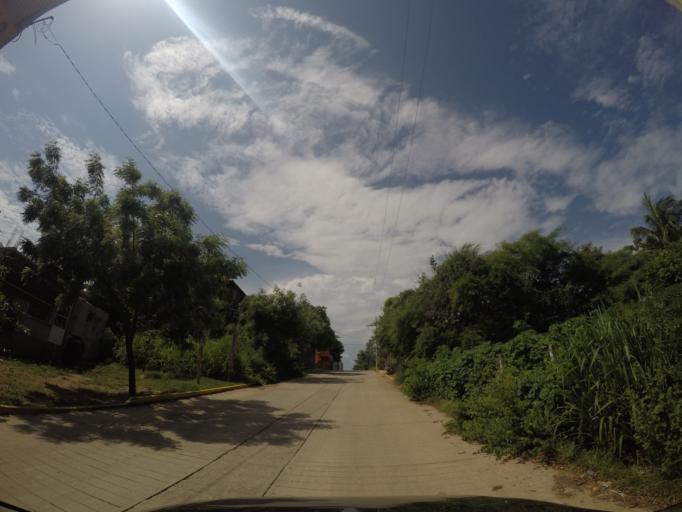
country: MX
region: Oaxaca
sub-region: Santa Maria Colotepec
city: Brisas de Zicatela
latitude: 15.8365
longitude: -97.0422
